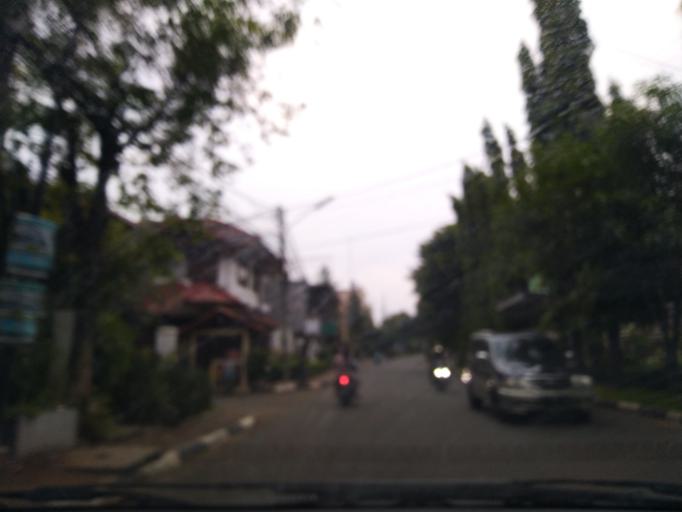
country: ID
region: Banten
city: South Tangerang
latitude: -6.2679
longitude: 106.7447
